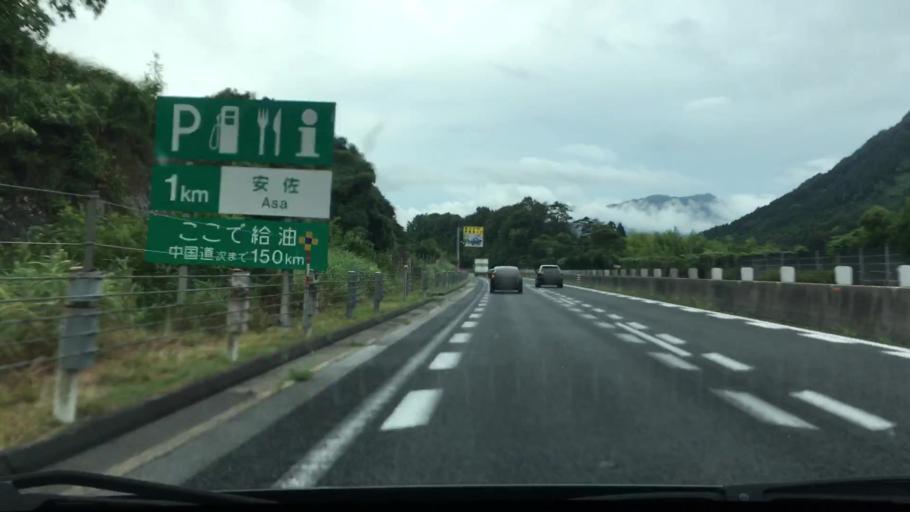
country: JP
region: Hiroshima
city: Hiroshima-shi
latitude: 34.5983
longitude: 132.4909
